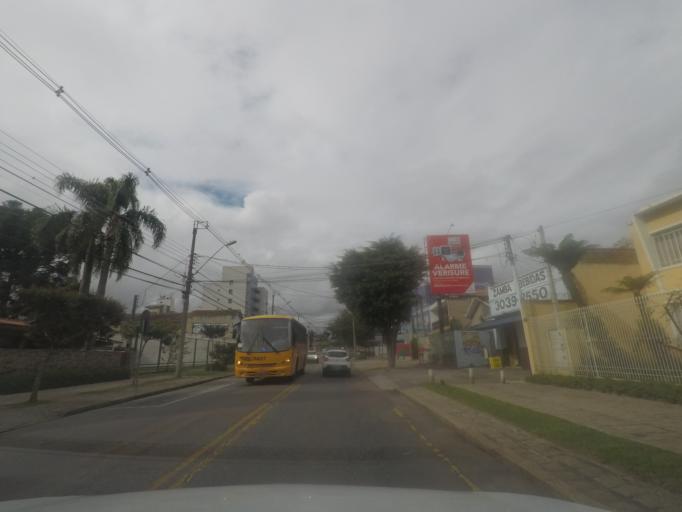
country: BR
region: Parana
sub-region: Curitiba
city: Curitiba
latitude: -25.4349
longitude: -49.2411
